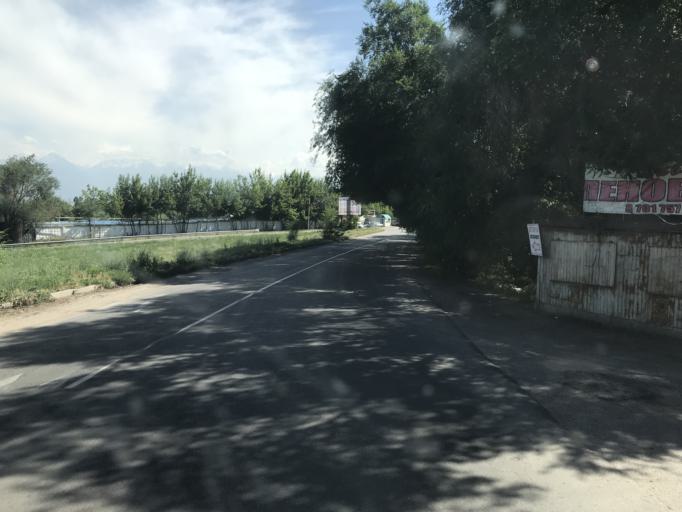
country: KZ
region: Almaty Oblysy
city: Pervomayskiy
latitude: 43.3509
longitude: 76.9054
